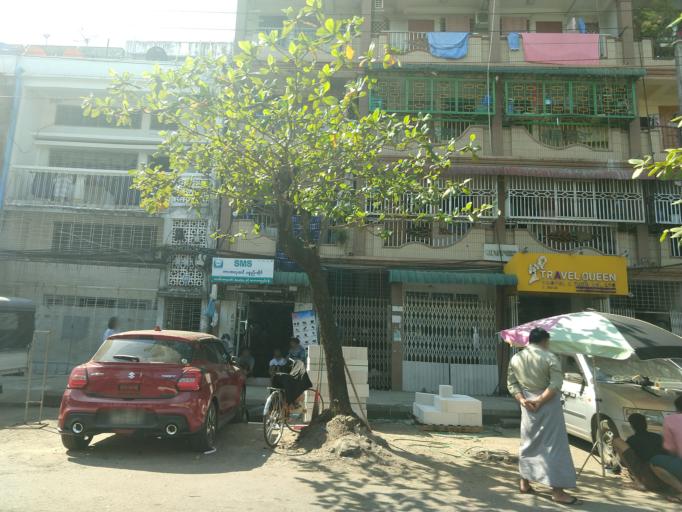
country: MM
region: Yangon
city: Yangon
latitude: 16.7731
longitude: 96.1726
